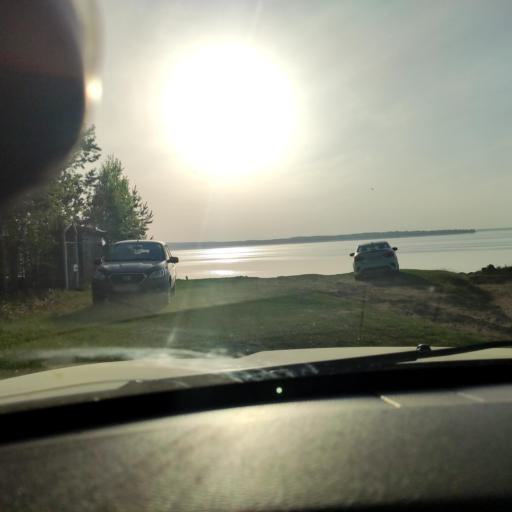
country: RU
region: Perm
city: Chermoz
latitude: 58.6002
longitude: 56.0994
